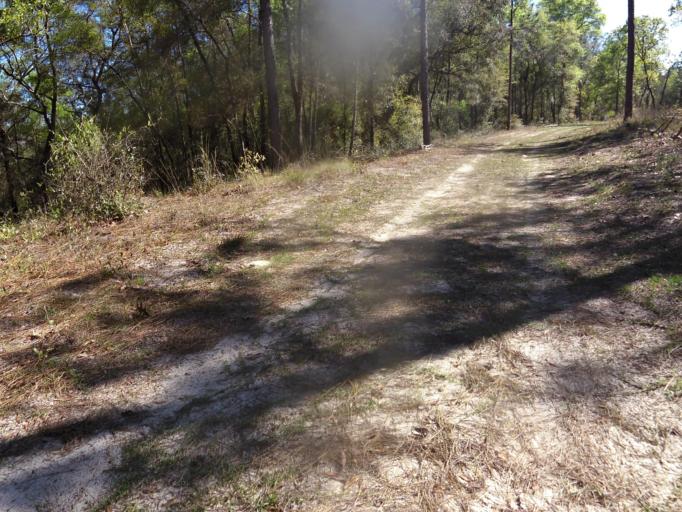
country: US
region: Florida
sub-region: Clay County
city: Keystone Heights
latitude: 29.8323
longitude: -82.0148
